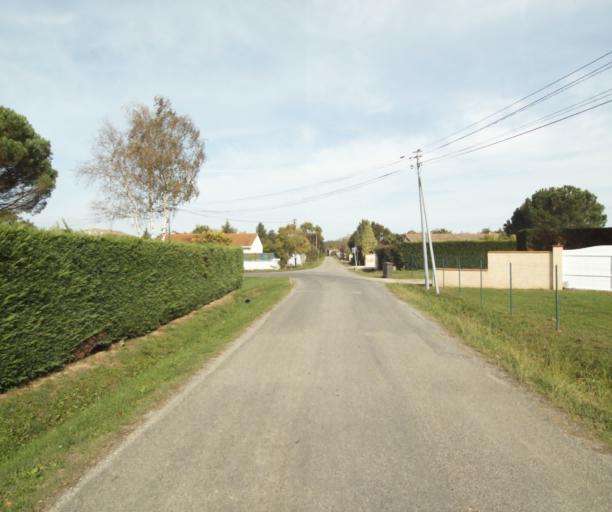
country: FR
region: Midi-Pyrenees
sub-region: Departement du Tarn-et-Garonne
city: Orgueil
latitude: 43.9118
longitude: 1.3952
